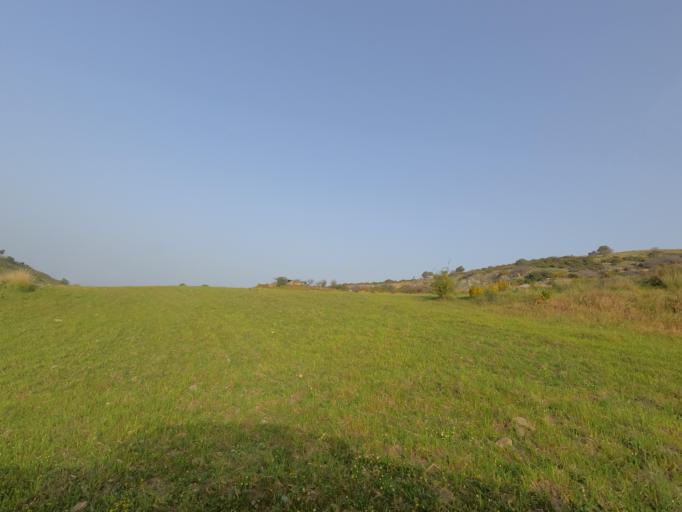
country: CY
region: Pafos
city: Polis
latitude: 34.9839
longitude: 32.3314
